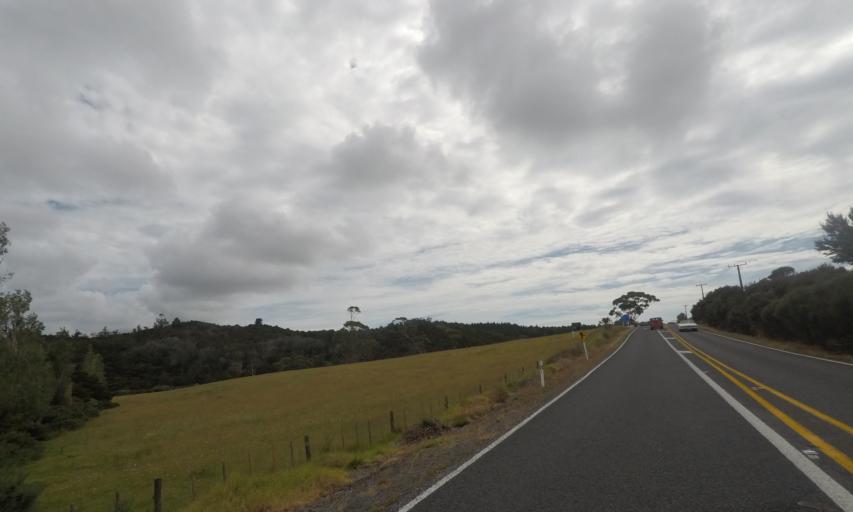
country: NZ
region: Northland
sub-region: Whangarei
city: Ruakaka
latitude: -35.7687
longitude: 174.4860
